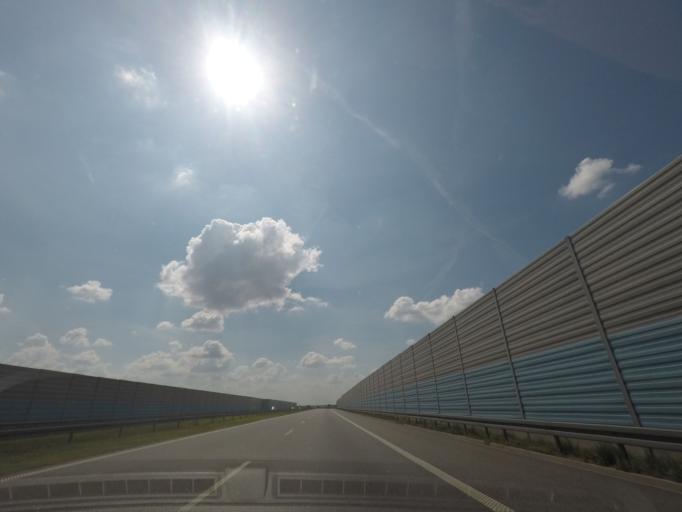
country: PL
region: Lodz Voivodeship
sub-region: powiat Lowicki
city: Lyszkowice
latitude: 52.0002
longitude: 19.9364
